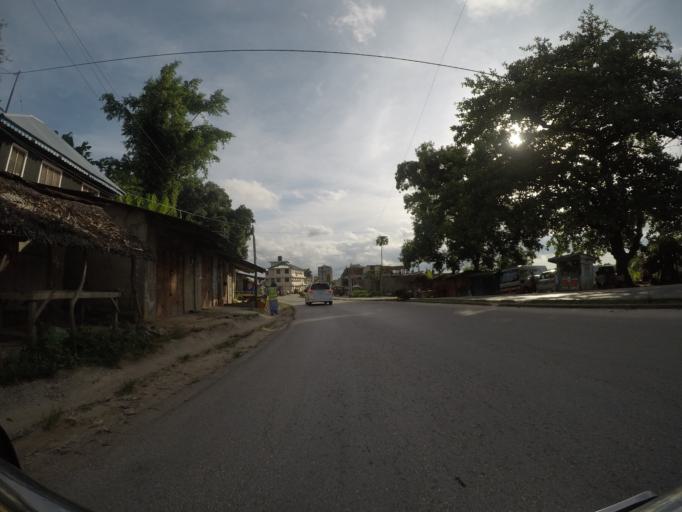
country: TZ
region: Pemba South
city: Chake Chake
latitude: -5.2400
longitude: 39.7696
